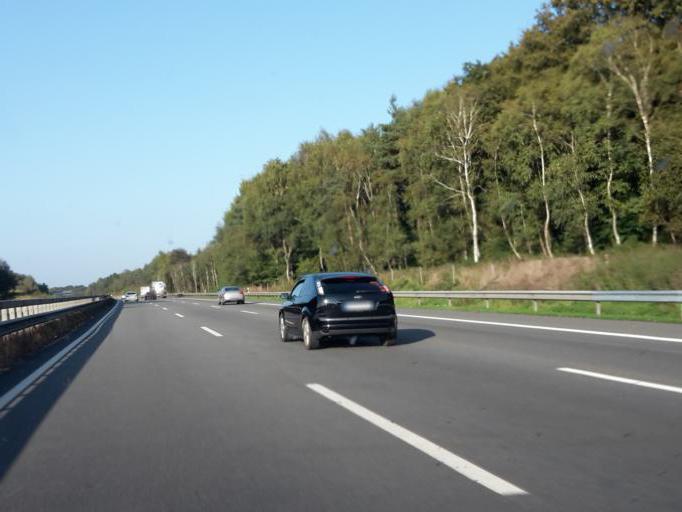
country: DE
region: Lower Saxony
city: Wallenhorst
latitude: 52.3578
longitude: 8.0372
